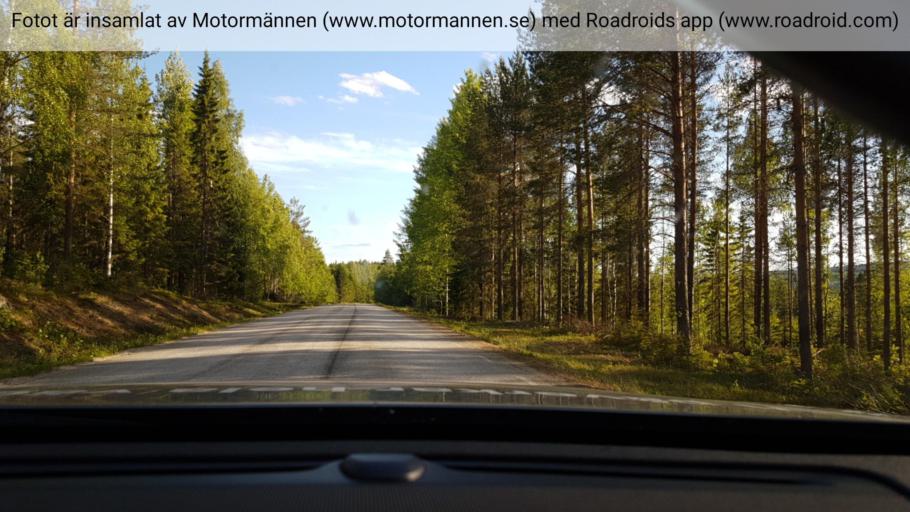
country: SE
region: Vaesterbotten
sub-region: Vannas Kommun
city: Vannasby
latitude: 63.9995
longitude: 19.9157
